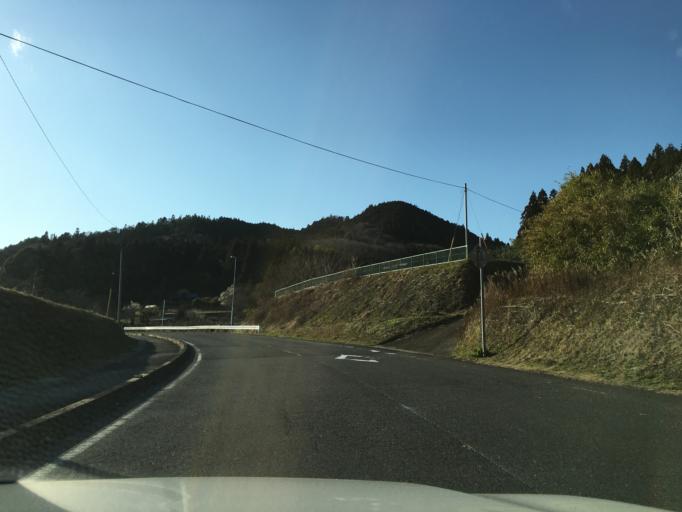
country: JP
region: Ibaraki
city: Daigo
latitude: 36.7805
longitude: 140.2726
